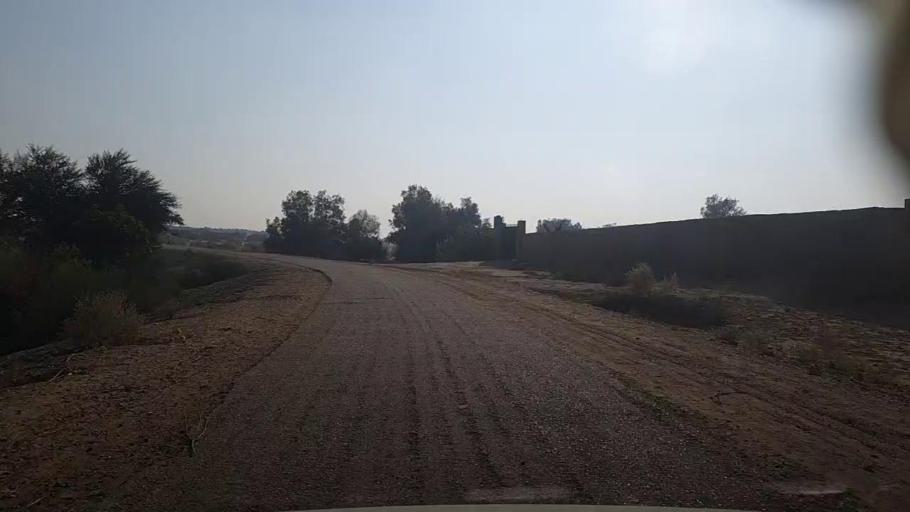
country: PK
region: Sindh
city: Kandiari
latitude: 26.8289
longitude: 68.4888
